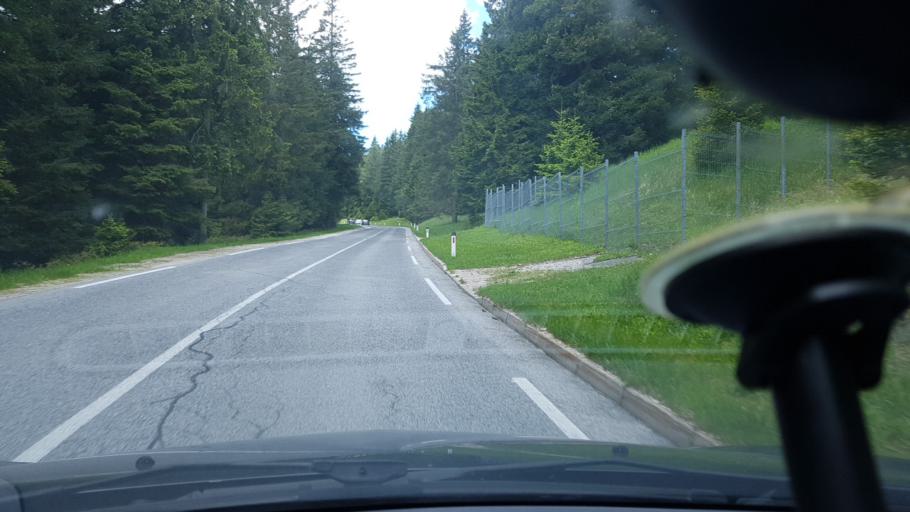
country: SI
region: Vitanje
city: Vitanje
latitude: 46.4475
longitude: 15.3293
